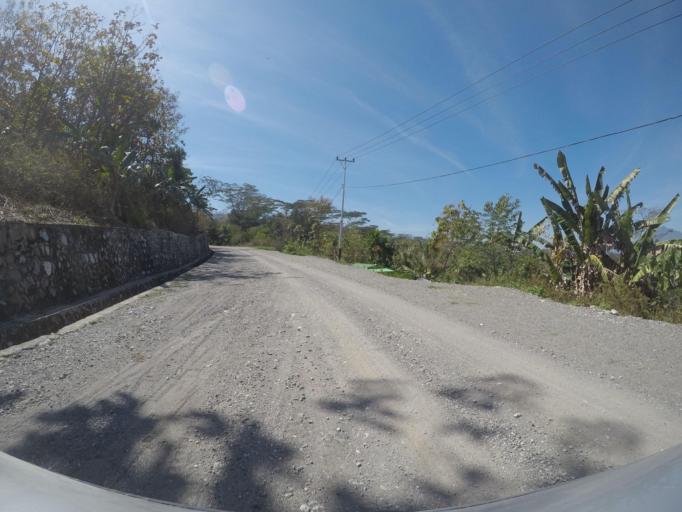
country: TL
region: Ermera
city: Gleno
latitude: -8.8068
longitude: 125.3125
